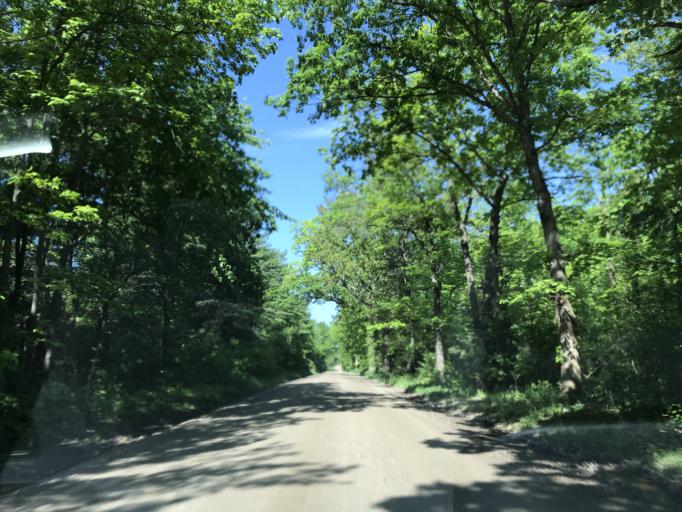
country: US
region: Michigan
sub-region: Oakland County
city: South Lyon
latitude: 42.4816
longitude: -83.6799
